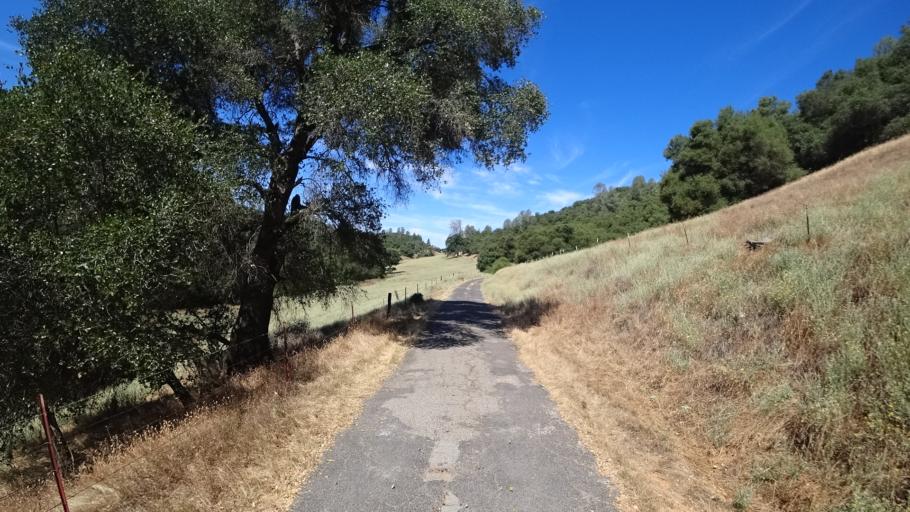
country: US
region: California
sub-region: Calaveras County
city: Murphys
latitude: 38.1439
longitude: -120.5249
